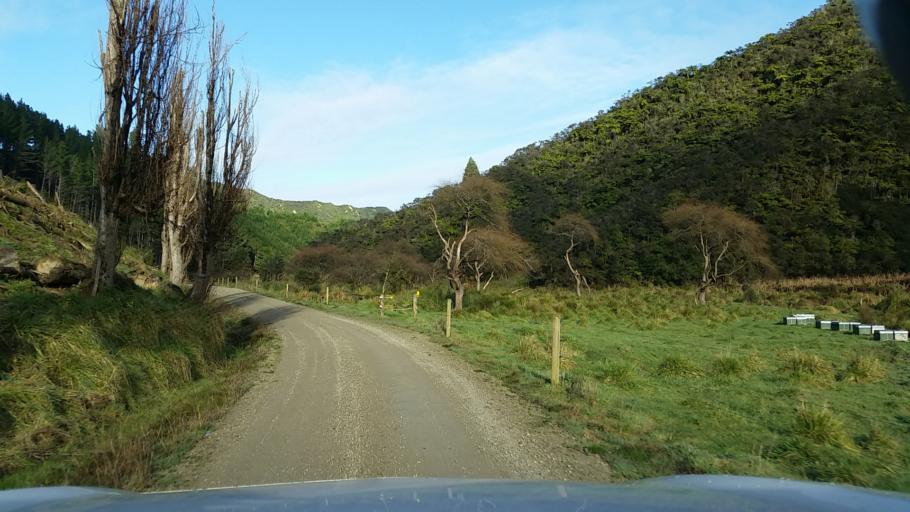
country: NZ
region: Taranaki
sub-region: South Taranaki District
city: Patea
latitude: -39.6869
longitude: 174.7622
